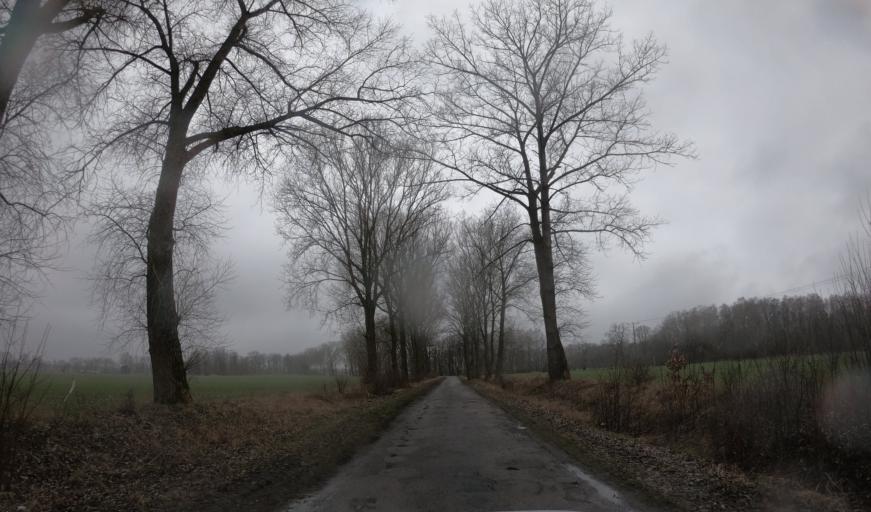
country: PL
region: West Pomeranian Voivodeship
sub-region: Powiat kamienski
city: Kamien Pomorski
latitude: 53.9079
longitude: 14.8344
